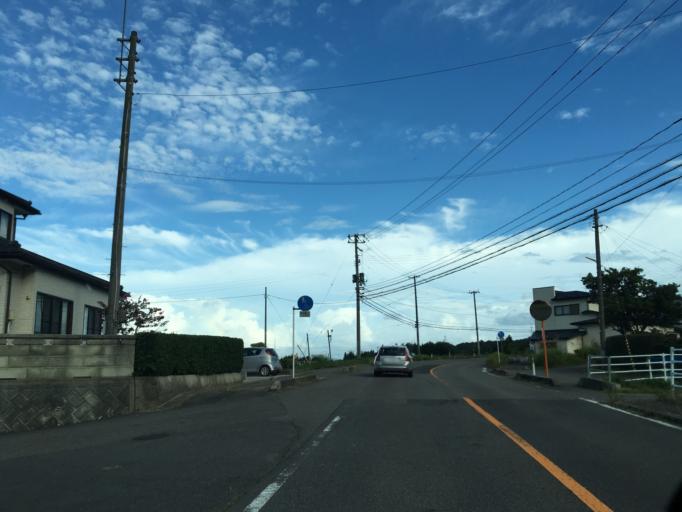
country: JP
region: Fukushima
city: Motomiya
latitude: 37.4983
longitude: 140.2797
